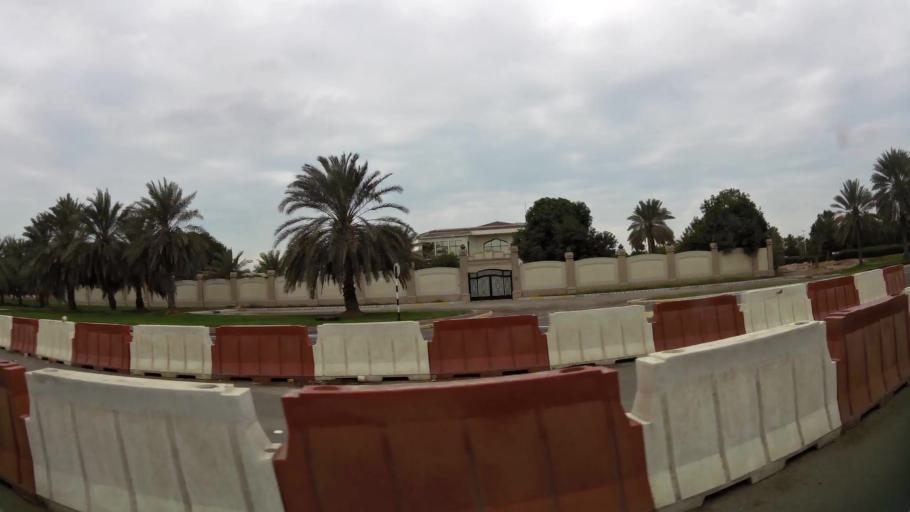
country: AE
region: Abu Dhabi
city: Abu Dhabi
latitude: 24.4312
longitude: 54.3722
